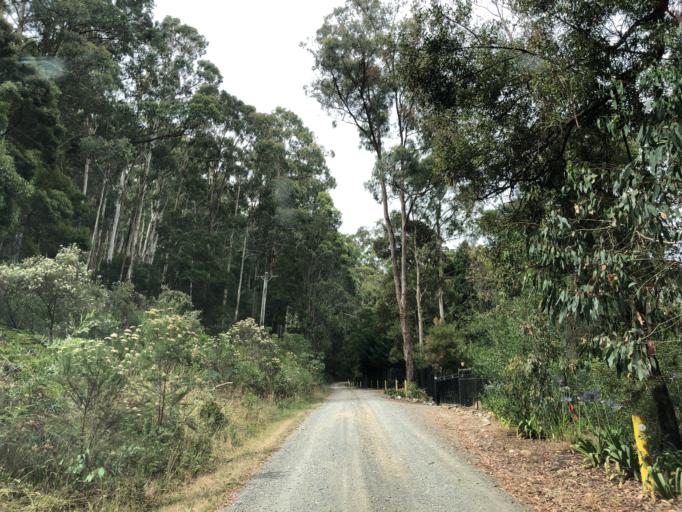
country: AU
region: Victoria
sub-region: Moorabool
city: Bacchus Marsh
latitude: -37.4731
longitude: 144.3245
